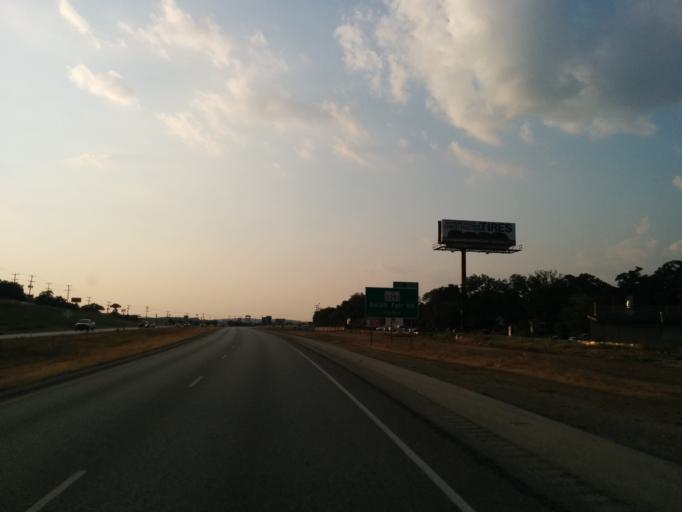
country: US
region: Texas
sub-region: Bexar County
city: Cross Mountain
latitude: 29.6602
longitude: -98.6276
